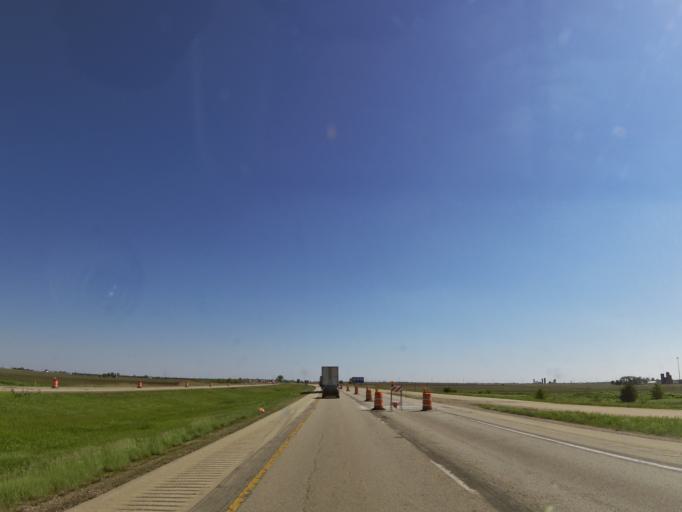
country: US
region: Illinois
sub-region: Ogle County
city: Hillcrest
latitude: 41.9648
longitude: -89.0235
